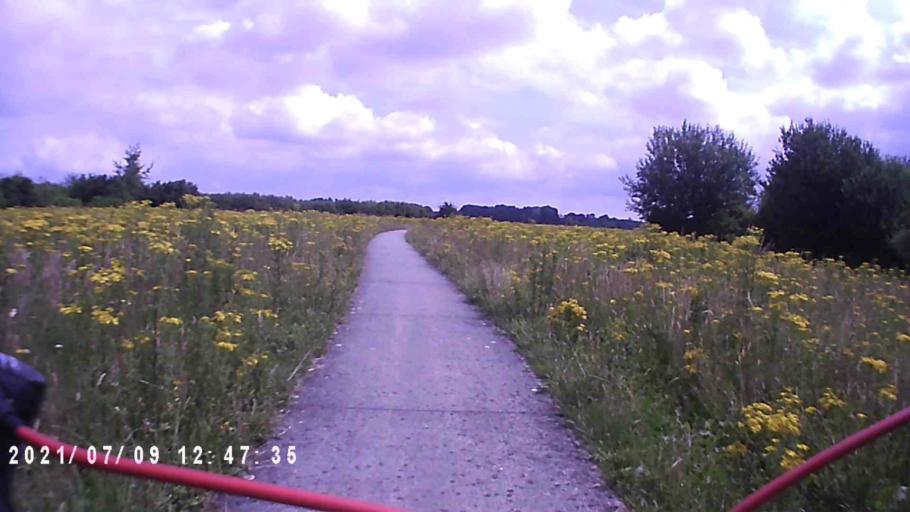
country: NL
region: Groningen
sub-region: Gemeente  Oldambt
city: Winschoten
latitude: 53.1269
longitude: 7.0337
